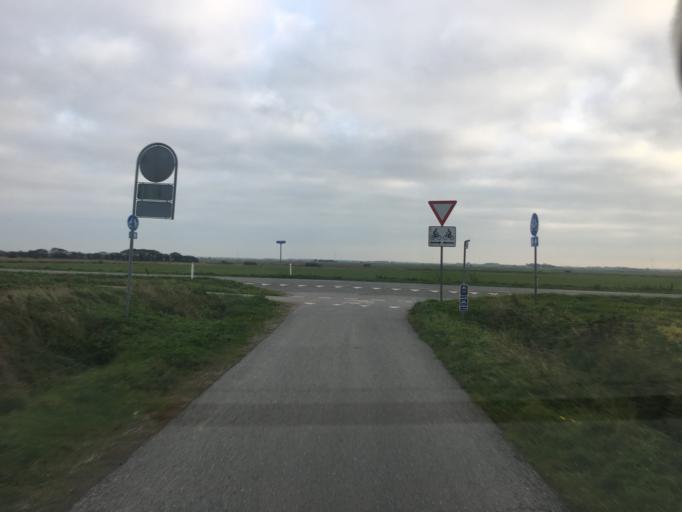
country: DE
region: Schleswig-Holstein
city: Rodenas
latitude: 54.9632
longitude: 8.7358
